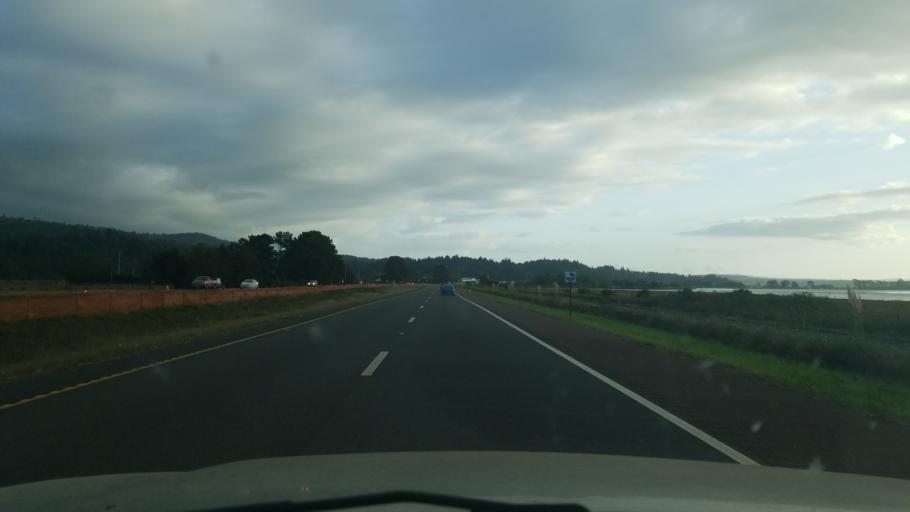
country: US
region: California
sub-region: Humboldt County
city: Bayside
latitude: 40.8385
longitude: -124.0822
